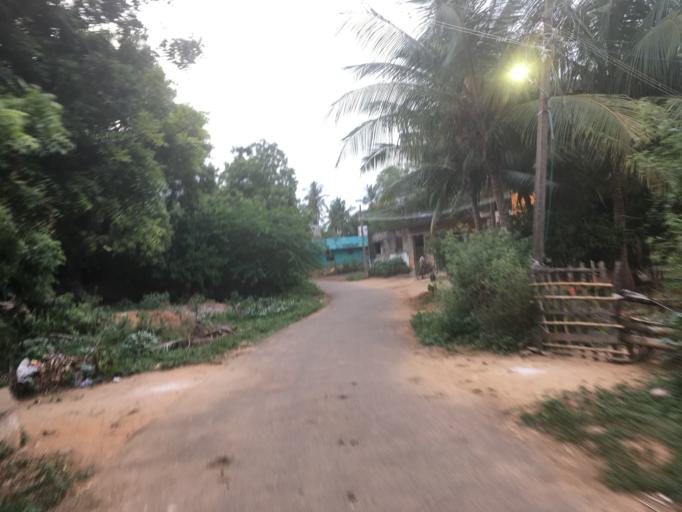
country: IN
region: Tamil Nadu
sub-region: Villupuram
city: Auroville
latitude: 12.0112
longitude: 79.8013
